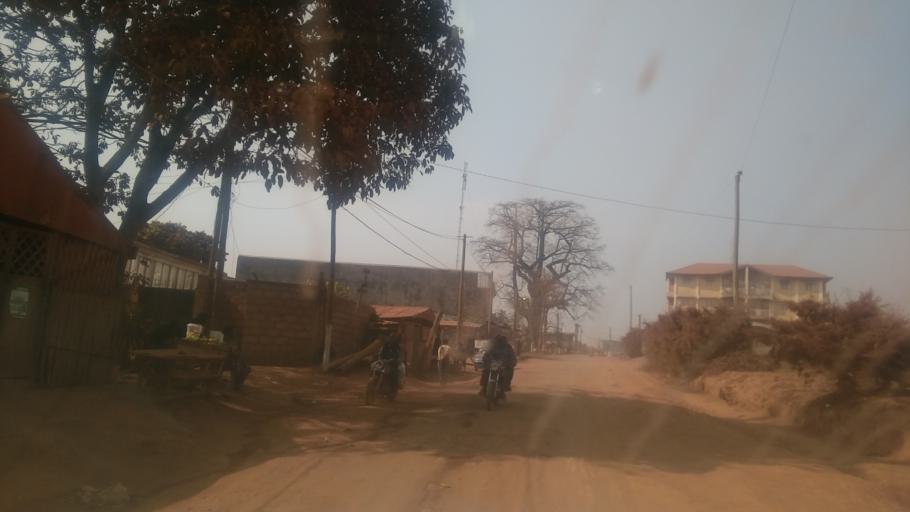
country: CM
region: West
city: Bafoussam
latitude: 5.5073
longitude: 10.4019
